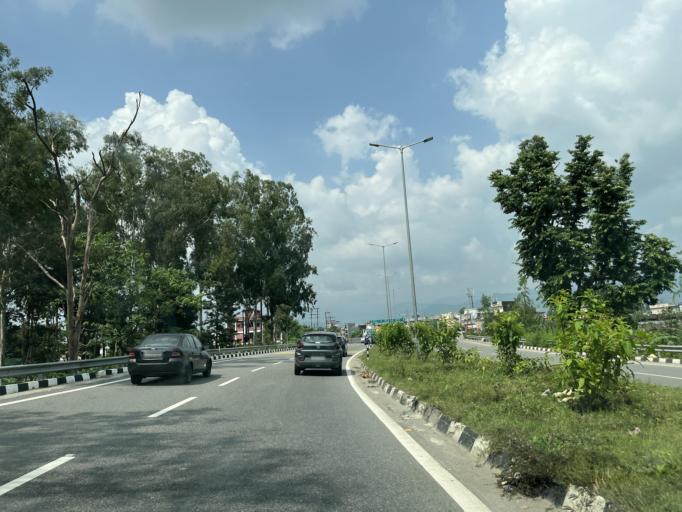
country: IN
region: Uttarakhand
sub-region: Dehradun
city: Raipur
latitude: 30.2514
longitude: 78.0933
